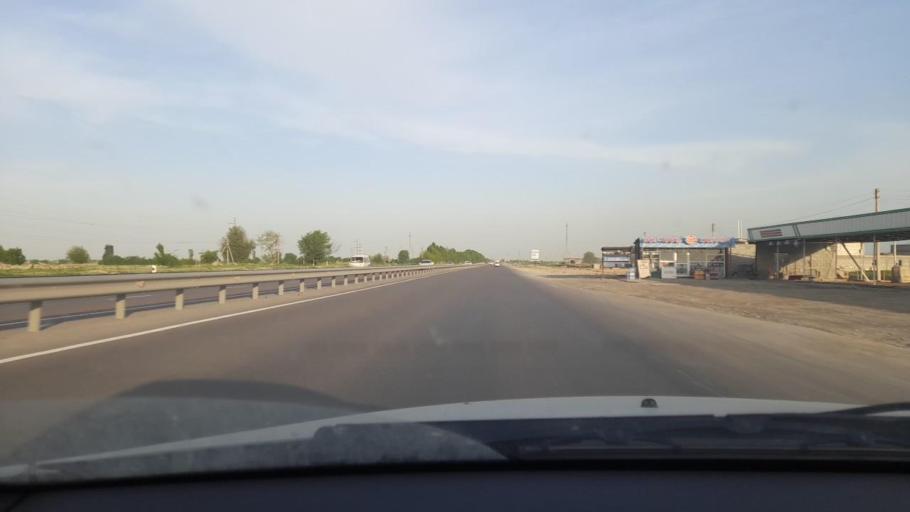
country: KZ
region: Ongtustik Qazaqstan
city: Myrzakent
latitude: 40.5367
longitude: 68.4275
